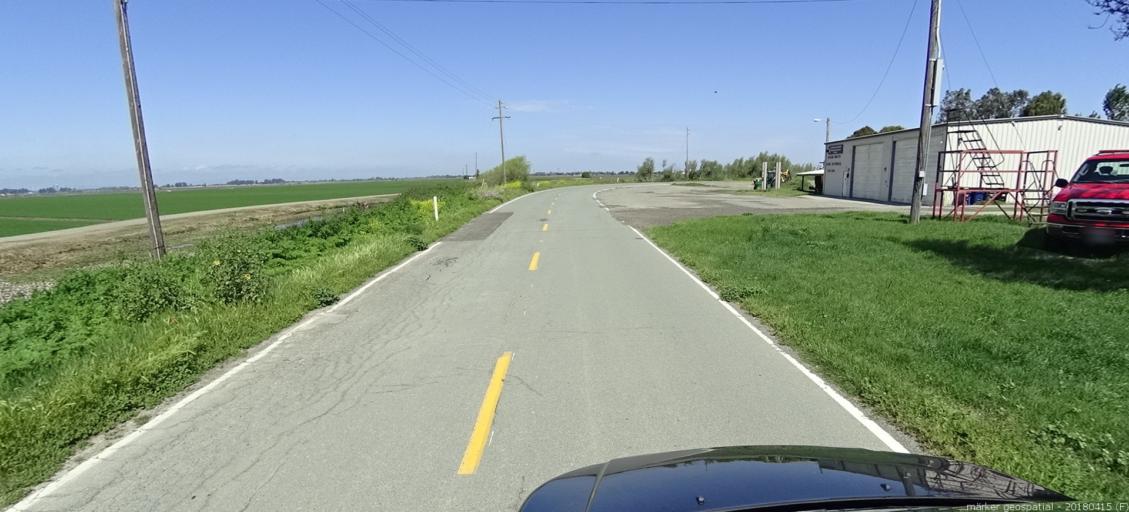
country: US
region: California
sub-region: Solano County
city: Rio Vista
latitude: 38.1421
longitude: -121.6240
